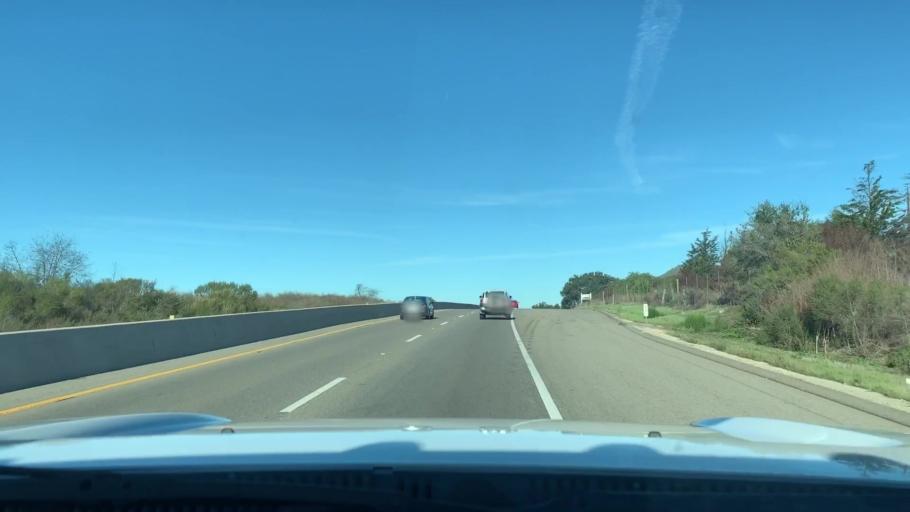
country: US
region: California
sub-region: San Luis Obispo County
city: Nipomo
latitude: 35.0802
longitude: -120.5263
